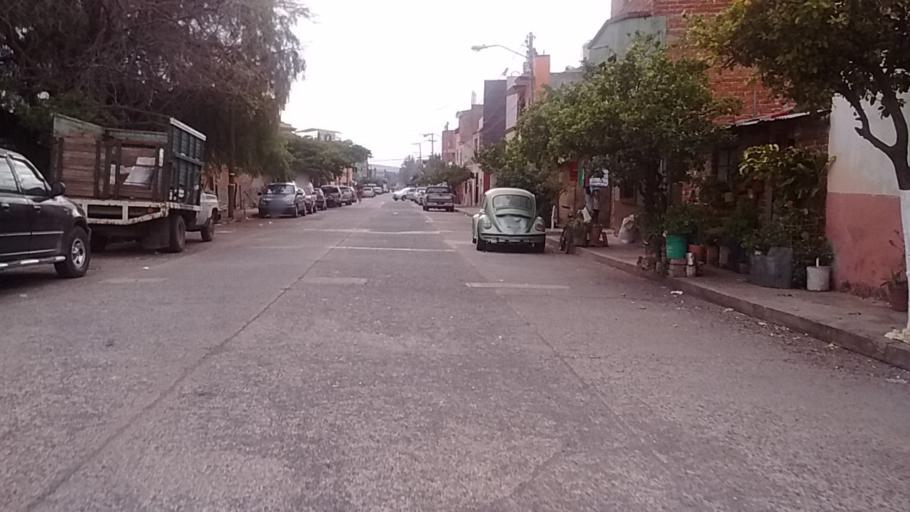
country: MX
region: Jalisco
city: Atotonilco el Alto
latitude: 20.5461
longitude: -102.5117
